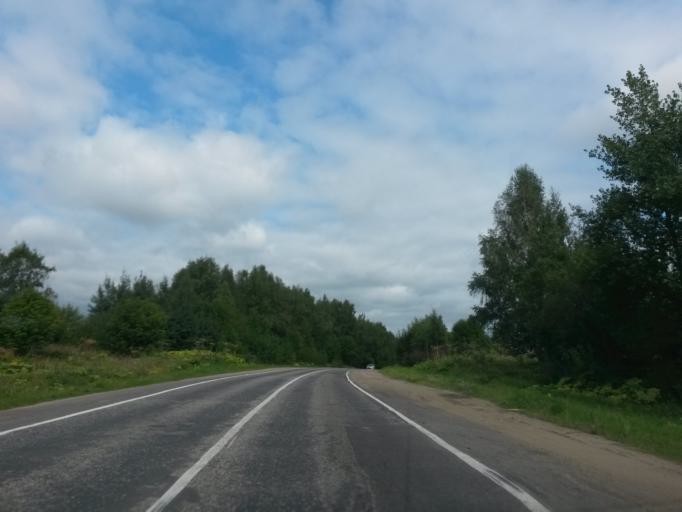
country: RU
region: Jaroslavl
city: Yaroslavl
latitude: 57.5437
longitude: 39.8621
